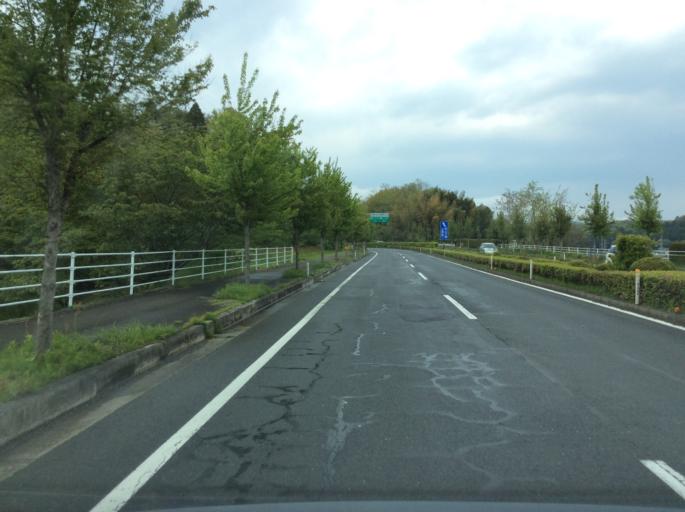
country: JP
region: Fukushima
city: Iwaki
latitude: 37.0653
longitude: 140.8490
